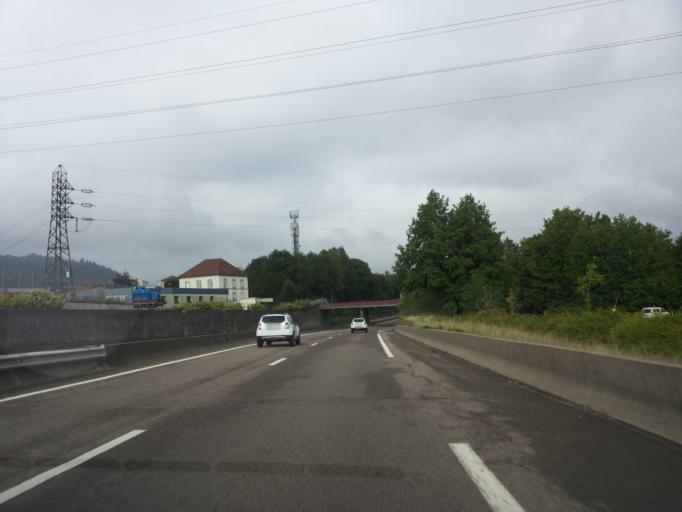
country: FR
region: Lorraine
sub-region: Departement des Vosges
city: Saint-Etienne-les-Remiremont
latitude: 48.0176
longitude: 6.6020
